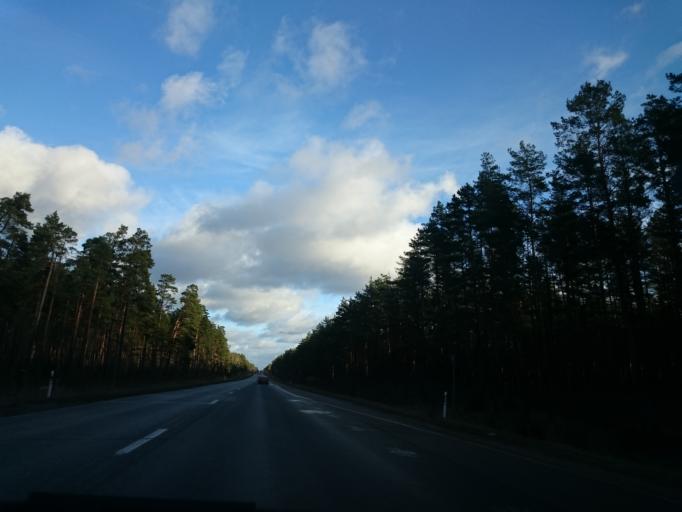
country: LV
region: Garkalne
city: Garkalne
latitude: 57.0635
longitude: 24.4731
